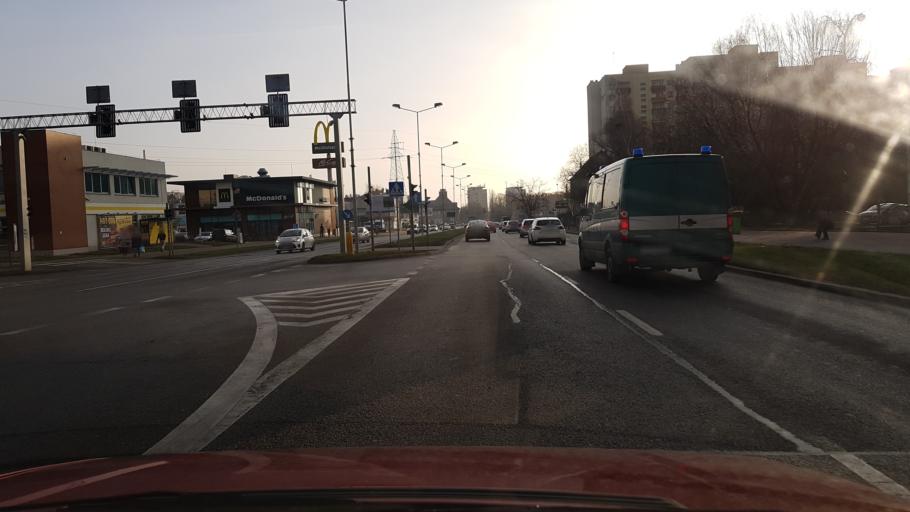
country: PL
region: West Pomeranian Voivodeship
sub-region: Szczecin
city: Szczecin
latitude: 53.4537
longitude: 14.5595
